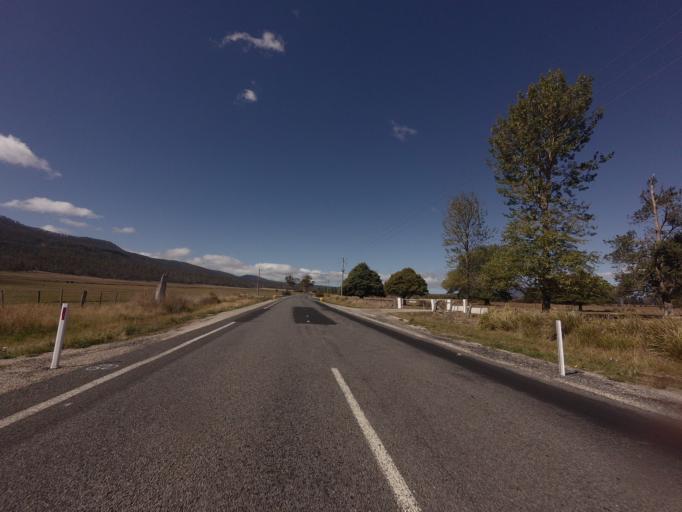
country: AU
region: Tasmania
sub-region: Break O'Day
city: St Helens
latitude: -41.5773
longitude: 148.1080
